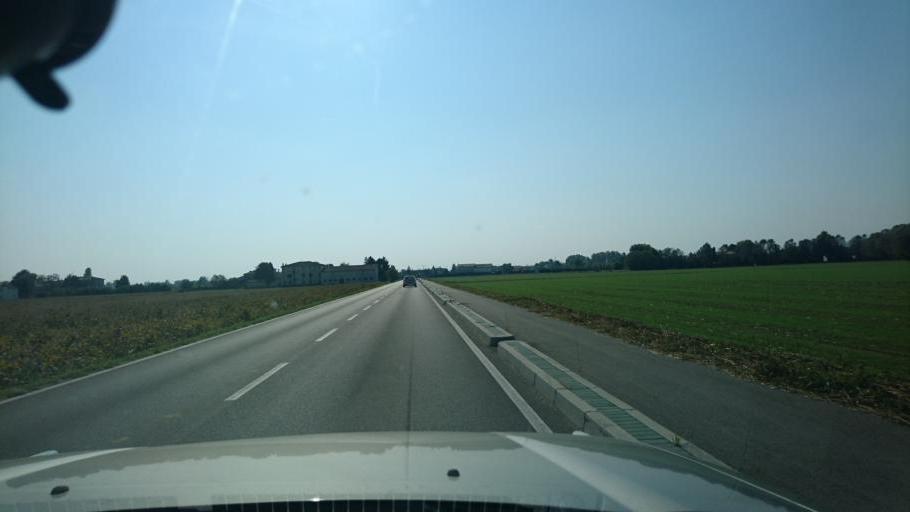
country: IT
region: Veneto
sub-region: Provincia di Padova
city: Gazzo
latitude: 45.5647
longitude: 11.7107
